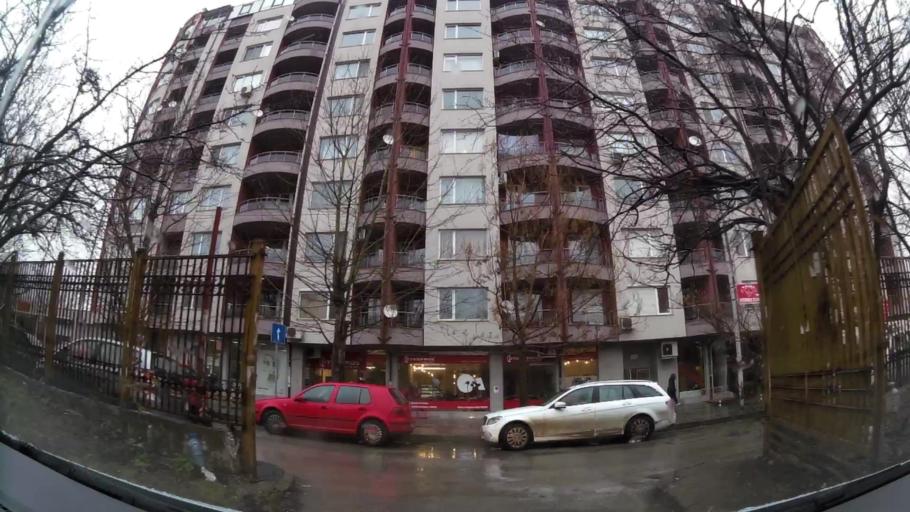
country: BG
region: Sofia-Capital
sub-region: Stolichna Obshtina
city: Sofia
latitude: 42.6498
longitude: 23.3403
